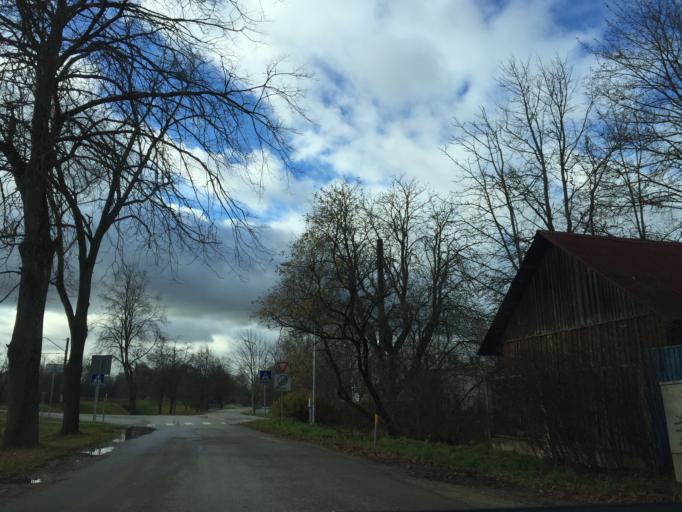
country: LV
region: Tukuma Rajons
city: Tukums
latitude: 56.9687
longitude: 23.1853
